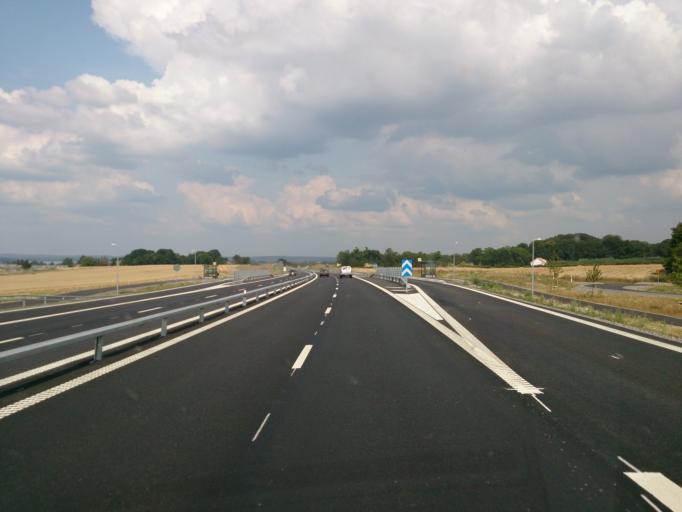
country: SE
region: Skane
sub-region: Hoors Kommun
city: Loberod
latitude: 55.8272
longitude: 13.5405
